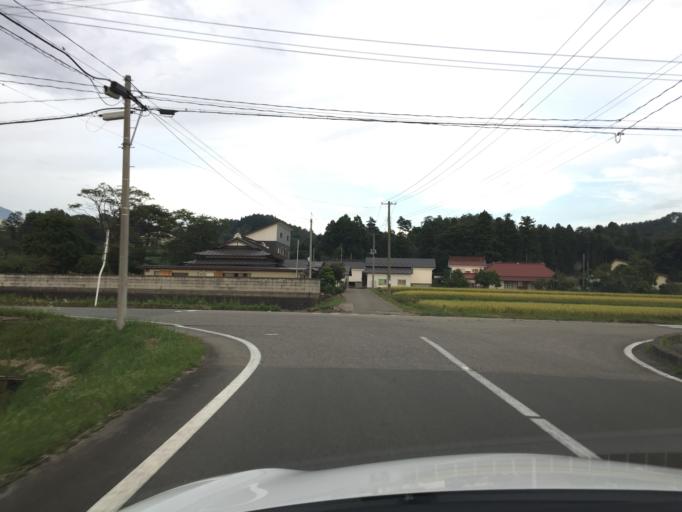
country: JP
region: Fukushima
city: Kitakata
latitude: 37.5448
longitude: 139.9504
